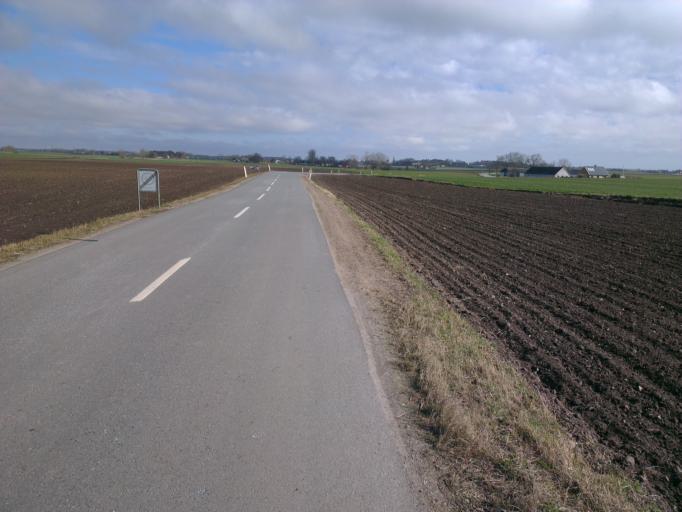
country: DK
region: Capital Region
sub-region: Frederikssund Kommune
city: Frederikssund
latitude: 55.8603
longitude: 12.1046
